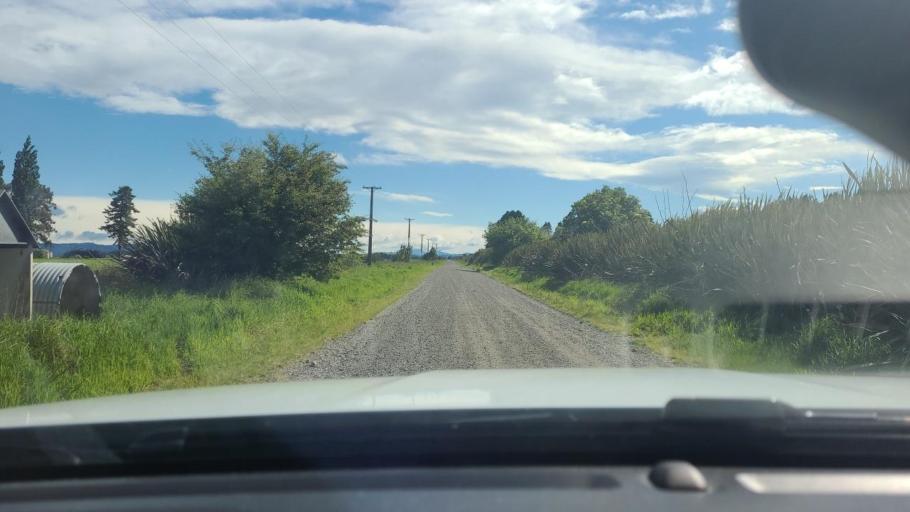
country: NZ
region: Southland
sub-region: Southland District
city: Winton
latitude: -46.1131
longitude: 168.2356
